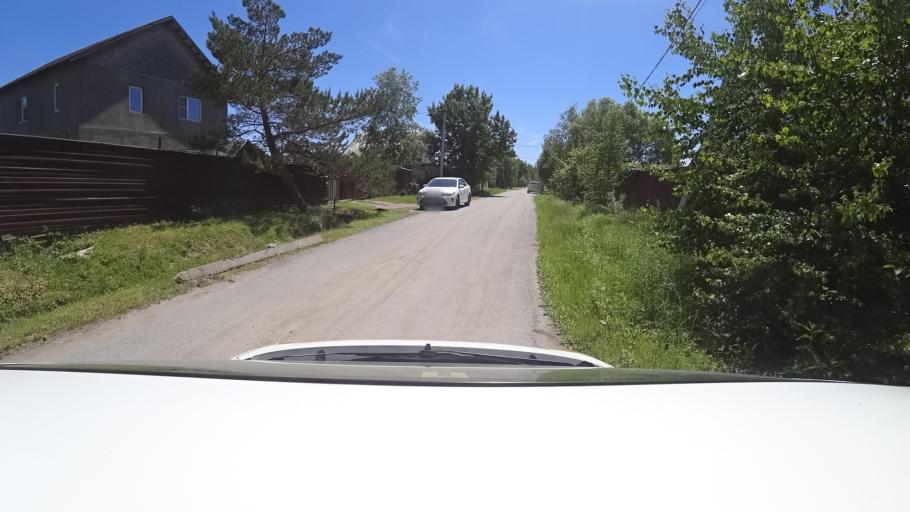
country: RU
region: Khabarovsk Krai
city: Topolevo
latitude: 48.5124
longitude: 135.1738
